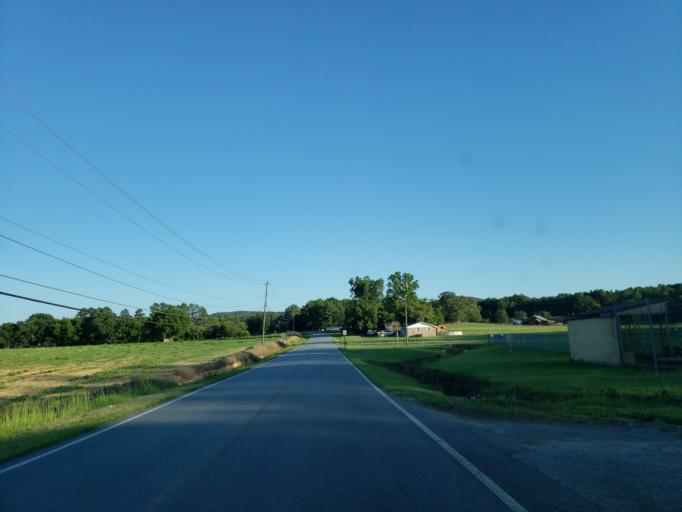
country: US
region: Georgia
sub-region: Bartow County
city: Euharlee
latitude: 34.0924
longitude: -84.9909
